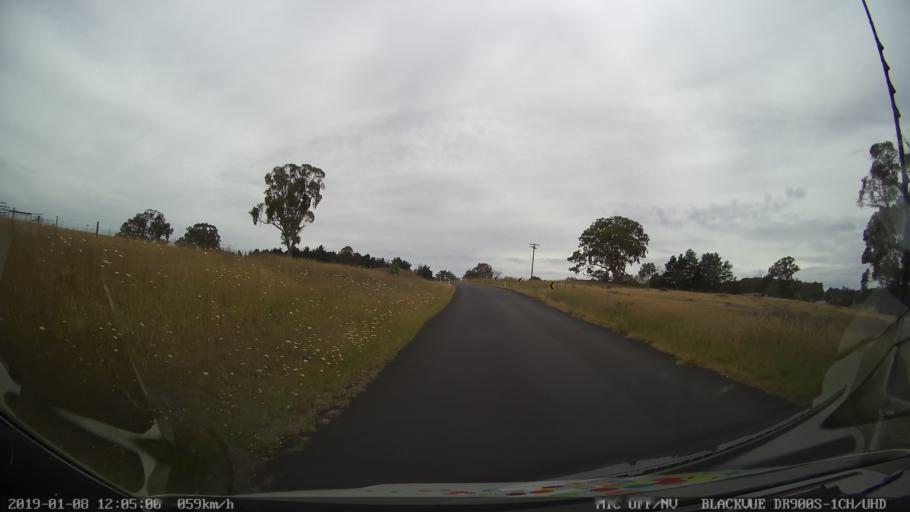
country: AU
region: New South Wales
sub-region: Armidale Dumaresq
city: Armidale
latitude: -30.4384
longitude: 151.5910
